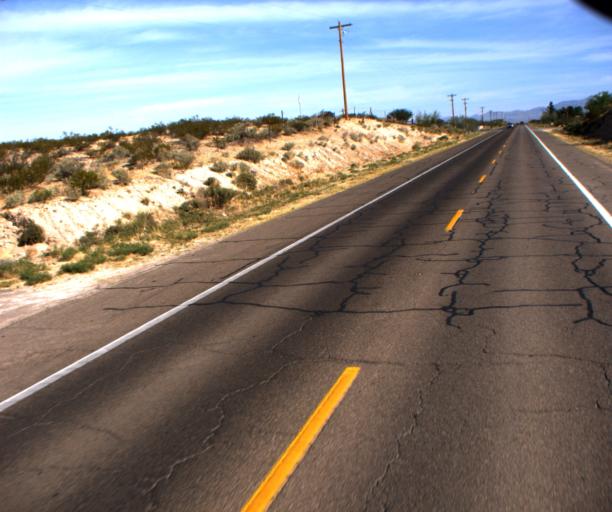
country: US
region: Arizona
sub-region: Graham County
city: Swift Trail Junction
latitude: 32.7037
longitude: -109.7078
